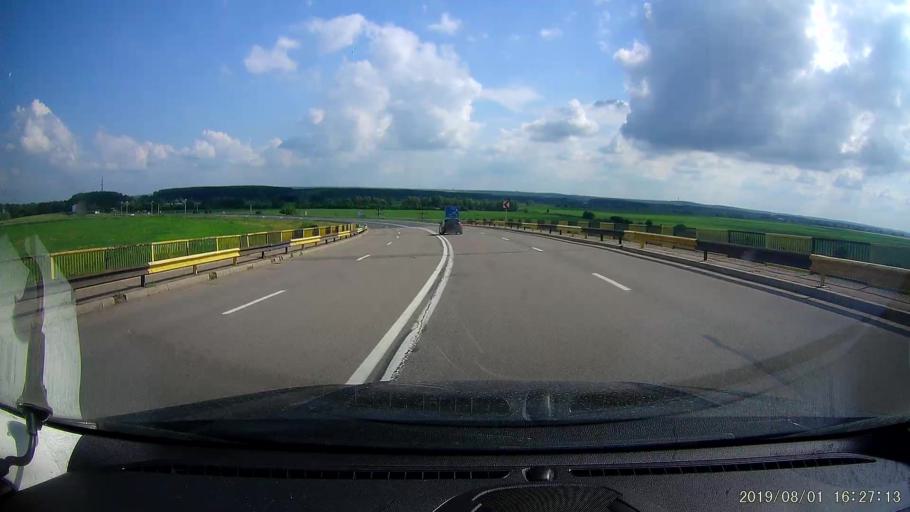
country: RO
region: Calarasi
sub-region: Municipiul Calarasi
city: Calarasi
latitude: 44.1663
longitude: 27.3108
